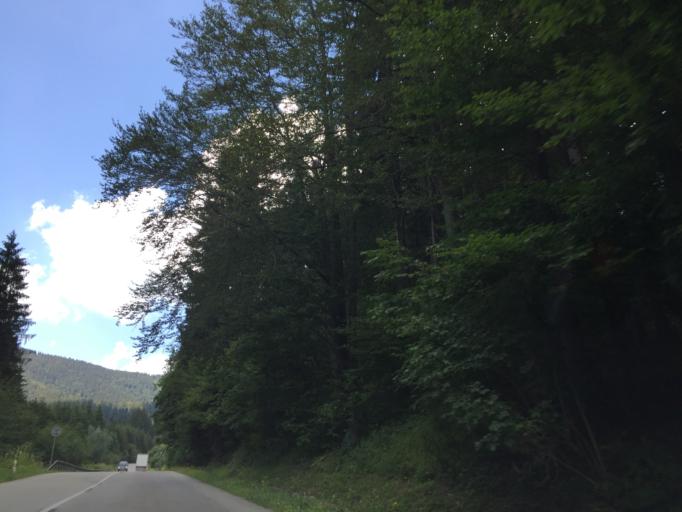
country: SK
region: Zilinsky
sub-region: Okres Dolny Kubin
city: Dolny Kubin
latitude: 49.2751
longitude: 19.3494
